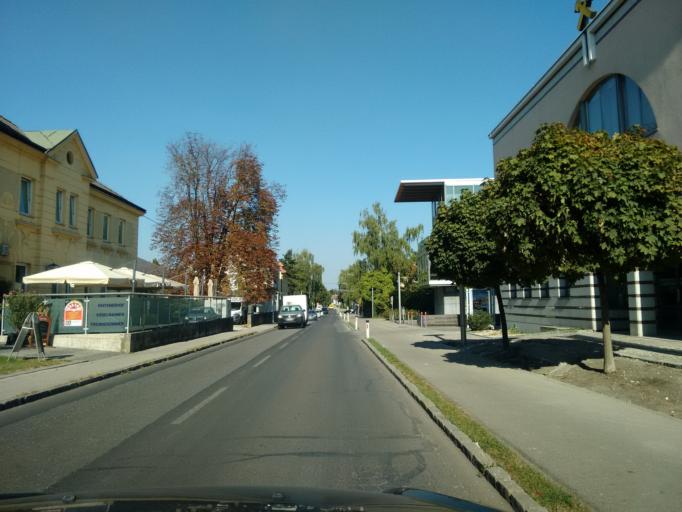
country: AT
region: Upper Austria
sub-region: Politischer Bezirk Linz-Land
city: Traun
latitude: 48.2222
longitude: 14.2395
